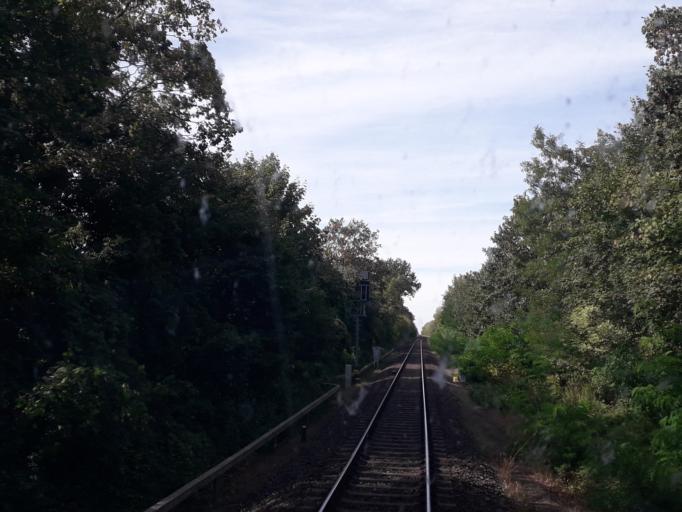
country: DE
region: Brandenburg
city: Velten
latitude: 52.6893
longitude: 13.1655
